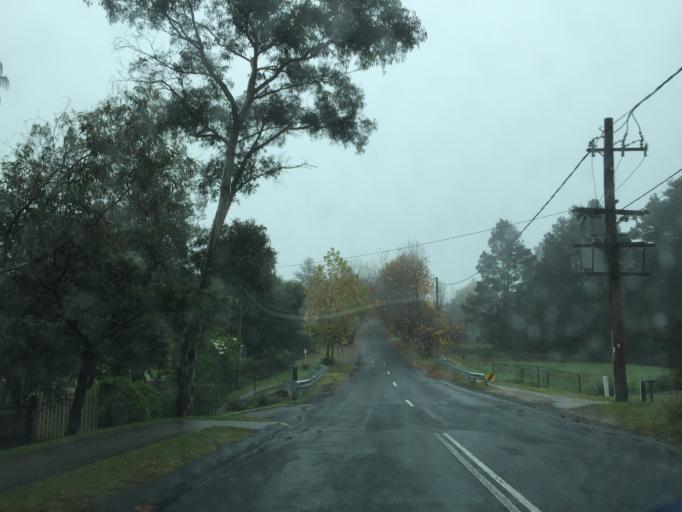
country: AU
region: New South Wales
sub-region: Blue Mountains Municipality
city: Leura
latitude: -33.7066
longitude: 150.3758
